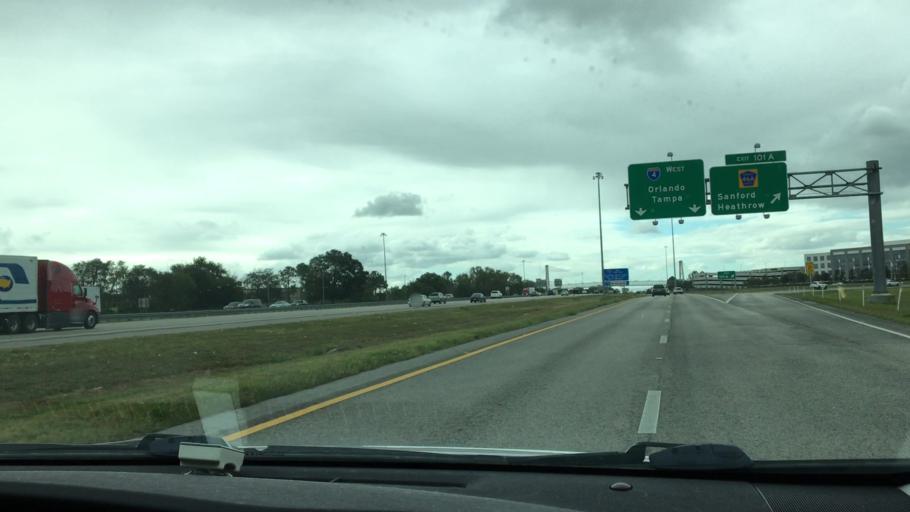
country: US
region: Florida
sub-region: Seminole County
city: Heathrow
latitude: 28.7853
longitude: -81.3516
